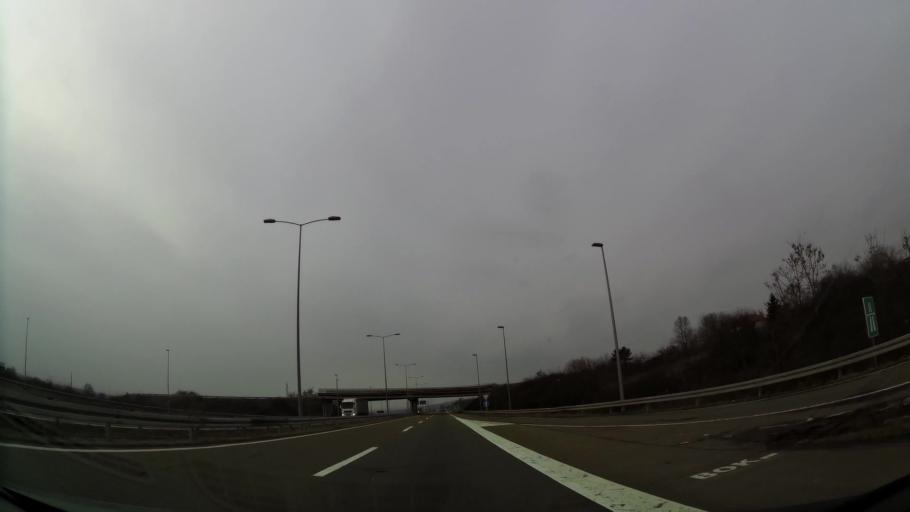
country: RS
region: Central Serbia
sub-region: Nisavski Okrug
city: Aleksinac
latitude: 43.5528
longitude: 21.6850
